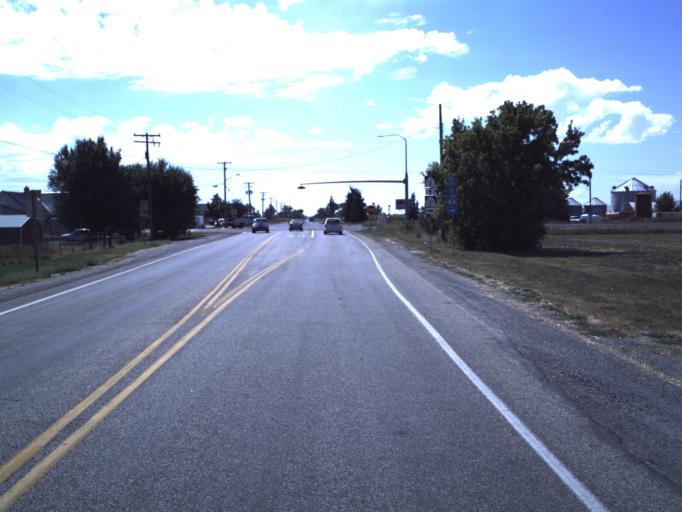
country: US
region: Utah
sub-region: Box Elder County
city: Garland
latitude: 41.7862
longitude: -112.1494
